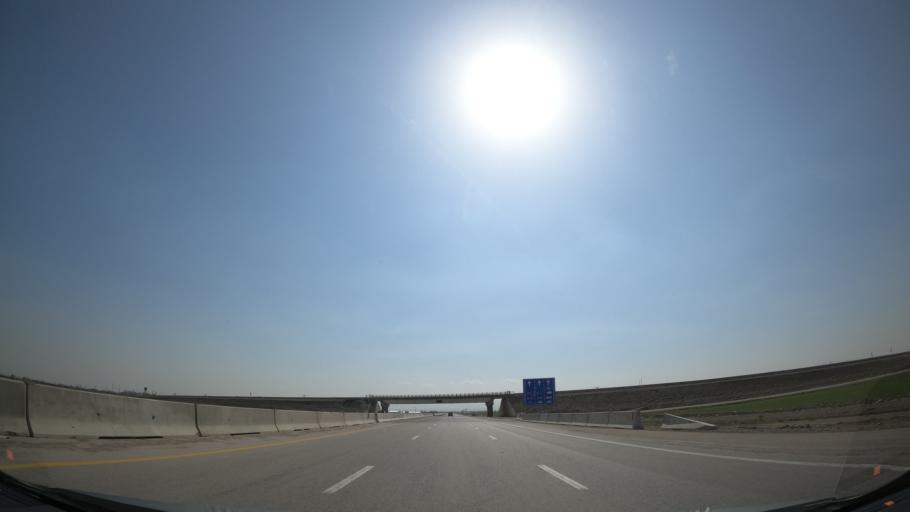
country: IR
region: Qazvin
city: Abyek
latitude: 36.0033
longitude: 50.4615
